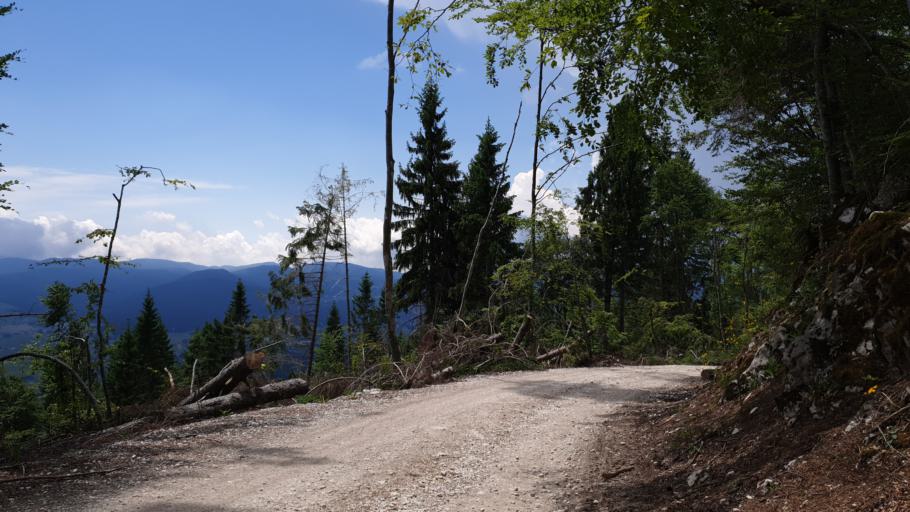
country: IT
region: Veneto
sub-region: Provincia di Vicenza
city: Canove di Roana
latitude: 45.8964
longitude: 11.4830
